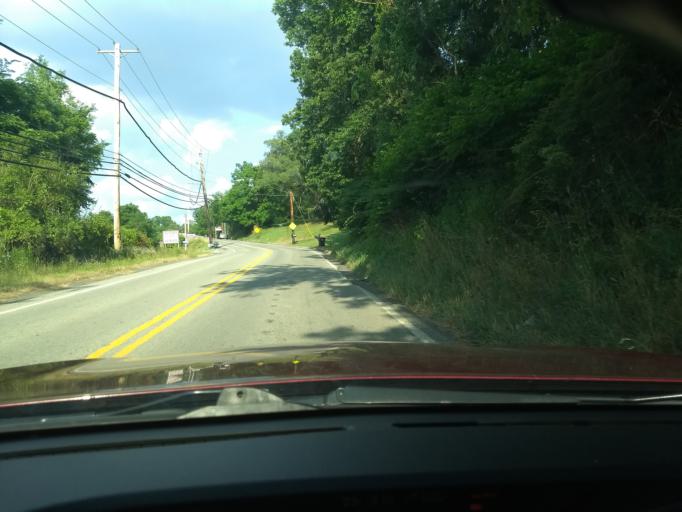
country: US
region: Pennsylvania
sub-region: Allegheny County
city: Plum
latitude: 40.4784
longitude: -79.7549
